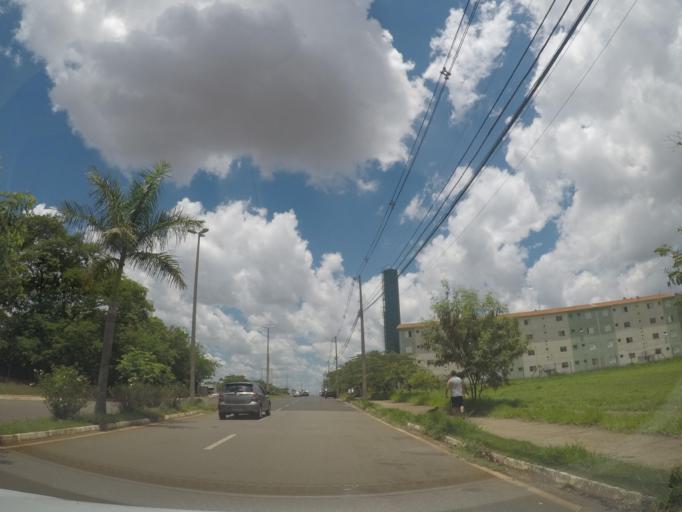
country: BR
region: Sao Paulo
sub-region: Hortolandia
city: Hortolandia
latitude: -22.8292
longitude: -47.2187
